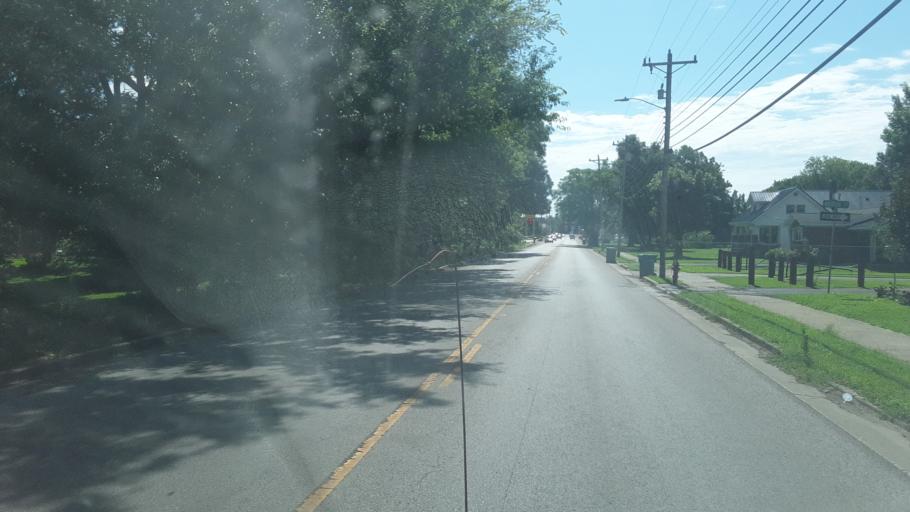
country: US
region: Kentucky
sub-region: Todd County
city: Elkton
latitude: 36.8107
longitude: -87.1593
